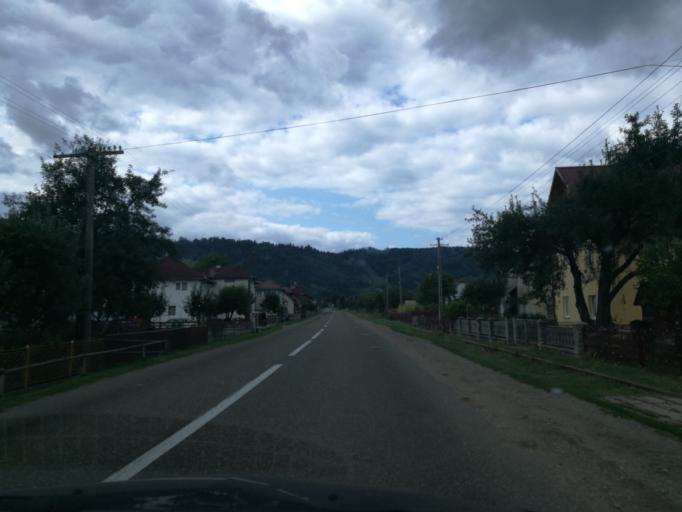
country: RO
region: Suceava
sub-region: Comuna Frumosu
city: Frumosu
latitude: 47.6169
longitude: 25.6305
